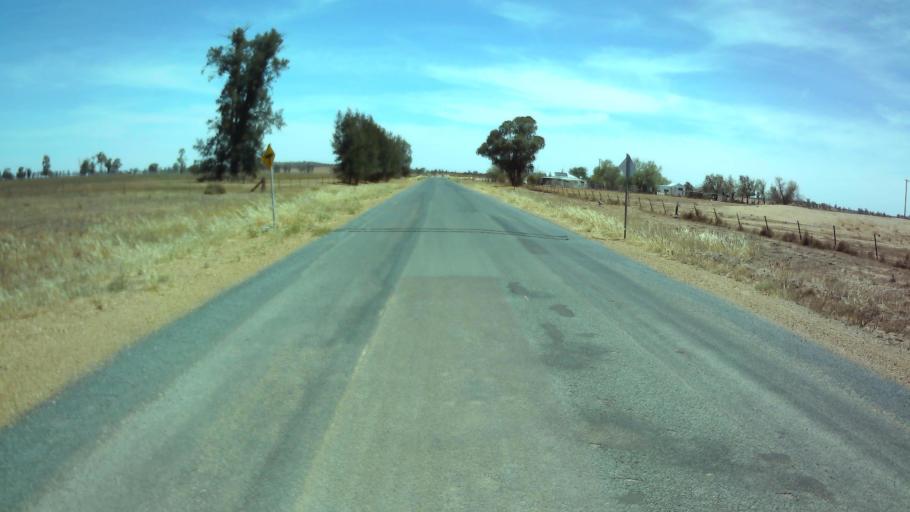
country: AU
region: New South Wales
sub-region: Weddin
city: Grenfell
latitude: -33.7482
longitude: 147.7678
